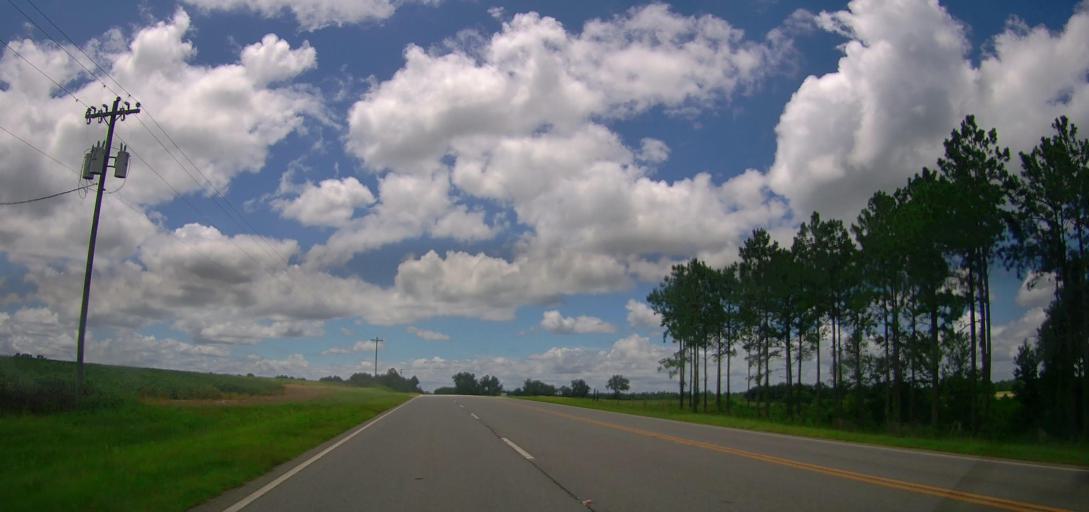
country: US
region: Georgia
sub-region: Turner County
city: Ashburn
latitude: 31.7220
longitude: -83.5345
